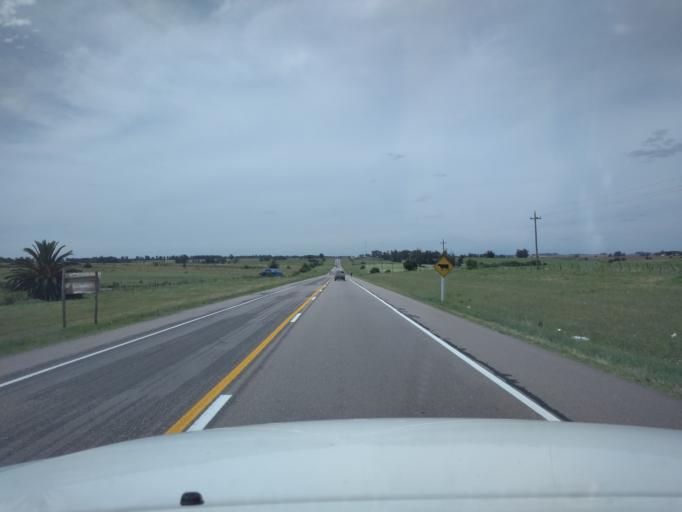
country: UY
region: Florida
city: Florida
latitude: -34.2249
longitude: -56.2105
